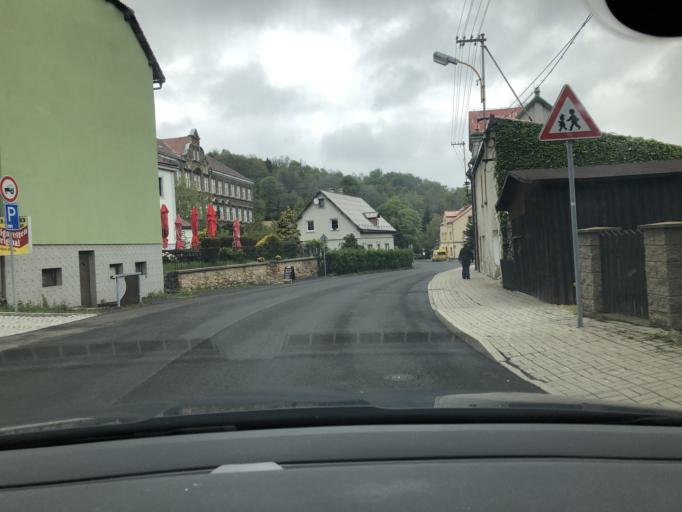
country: CZ
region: Ustecky
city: Libouchec
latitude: 50.7894
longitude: 13.9758
